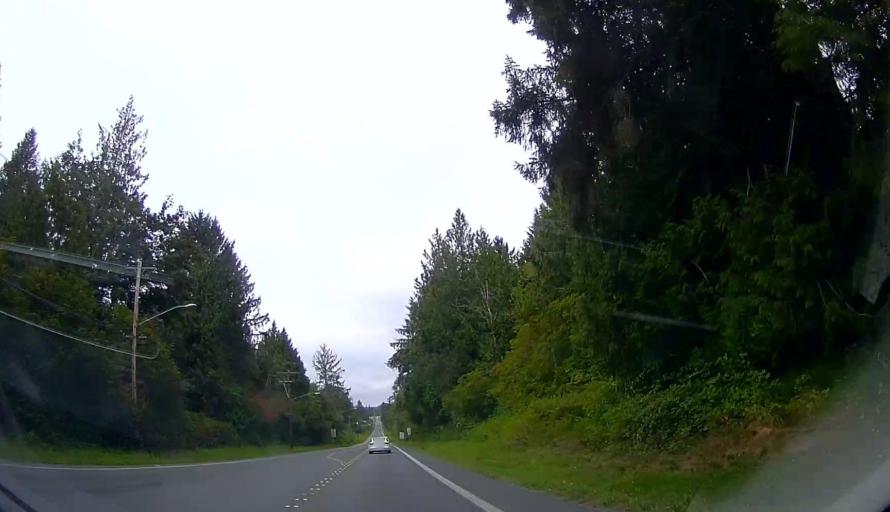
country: US
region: Washington
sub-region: Snohomish County
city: Tulalip
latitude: 48.0548
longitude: -122.2630
